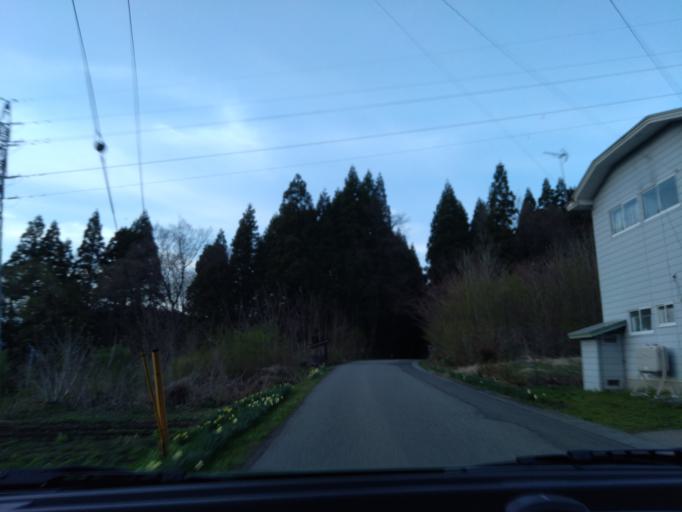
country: JP
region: Akita
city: Kakunodatemachi
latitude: 39.5906
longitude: 140.5777
